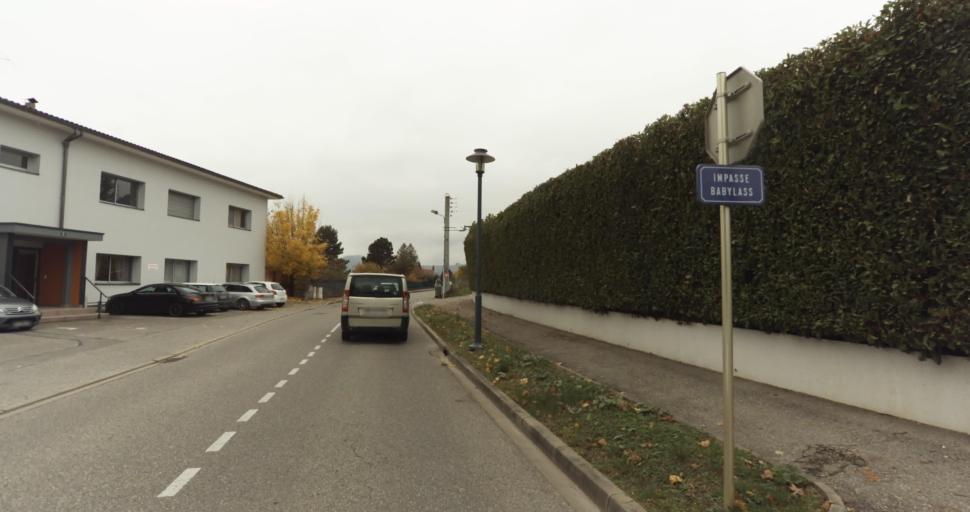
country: FR
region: Rhone-Alpes
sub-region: Departement de la Haute-Savoie
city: Annecy-le-Vieux
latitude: 45.9250
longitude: 6.1339
